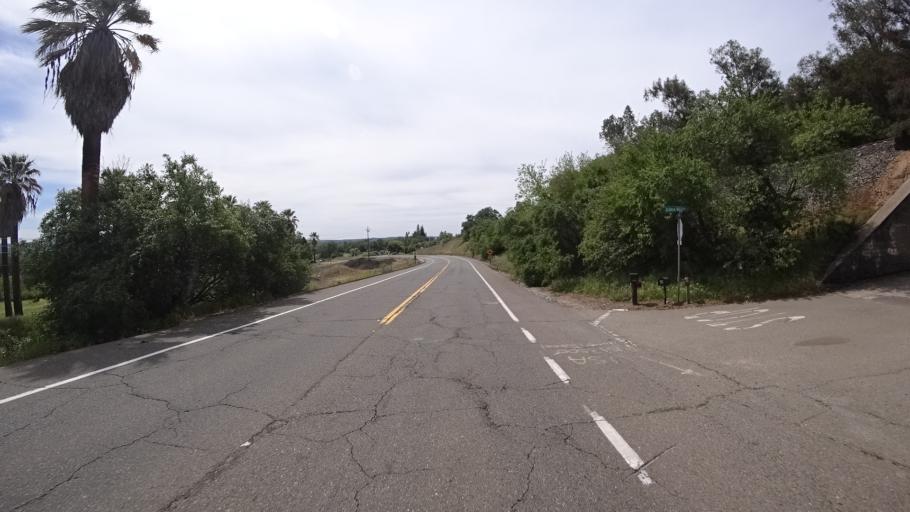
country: US
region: California
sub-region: Placer County
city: Loomis
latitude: 38.8375
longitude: -121.2203
